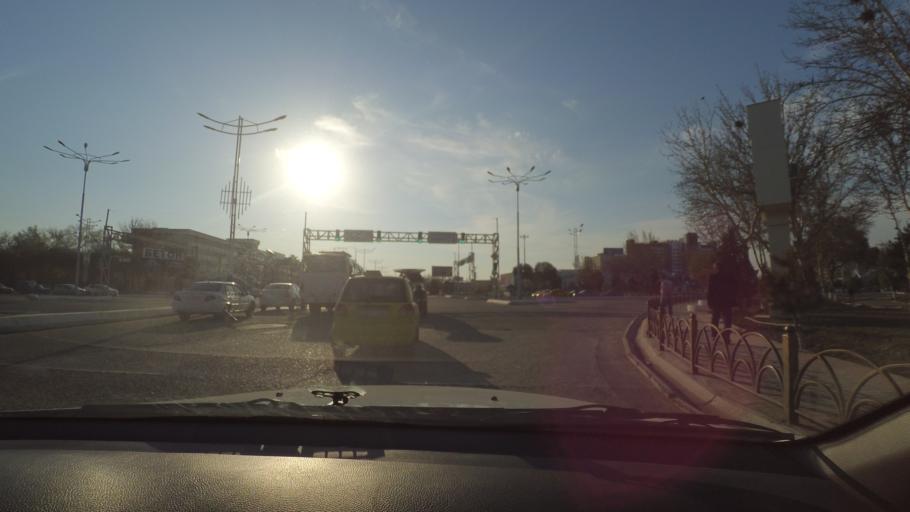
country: UZ
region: Bukhara
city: Bukhara
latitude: 39.7627
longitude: 64.4248
